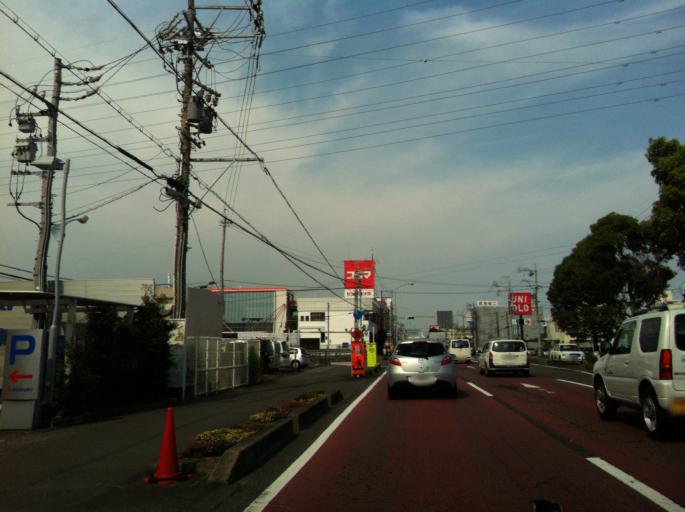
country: JP
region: Shizuoka
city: Shizuoka-shi
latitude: 34.9945
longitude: 138.4239
